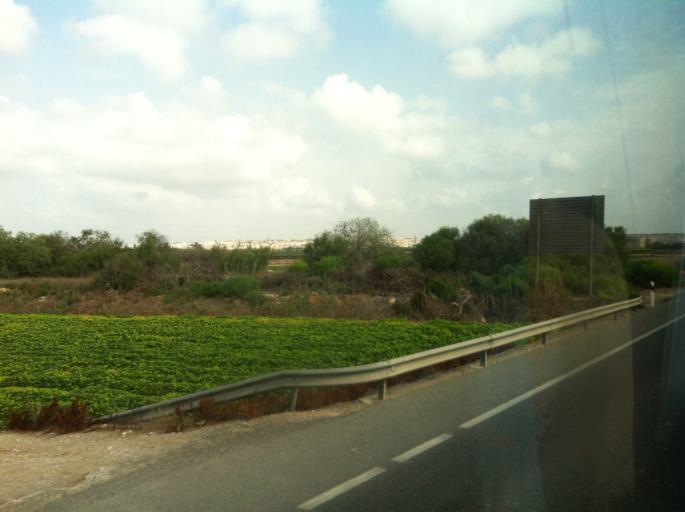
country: ES
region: Valencia
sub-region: Provincia de Alicante
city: Guardamar del Segura
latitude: 38.1016
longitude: -0.6633
